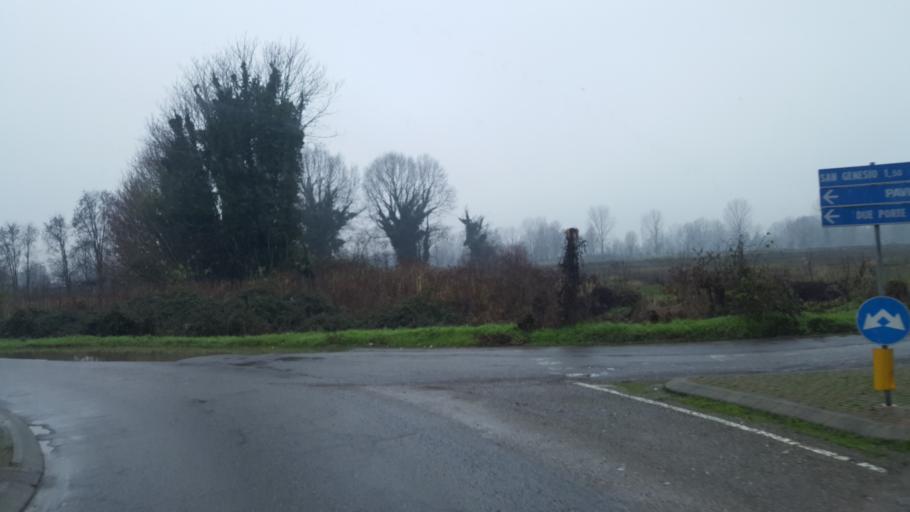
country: IT
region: Lombardy
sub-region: Provincia di Pavia
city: Sant'Alessio Con Vialone
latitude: 45.2213
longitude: 9.2059
